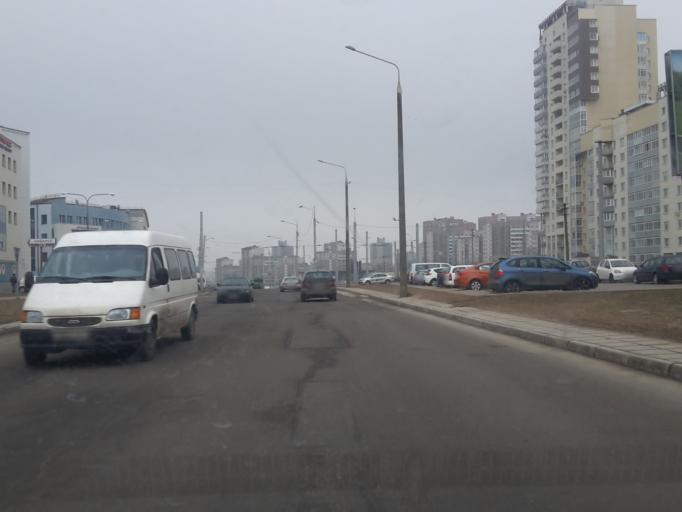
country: BY
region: Minsk
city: Novoye Medvezhino
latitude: 53.8906
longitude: 27.4280
